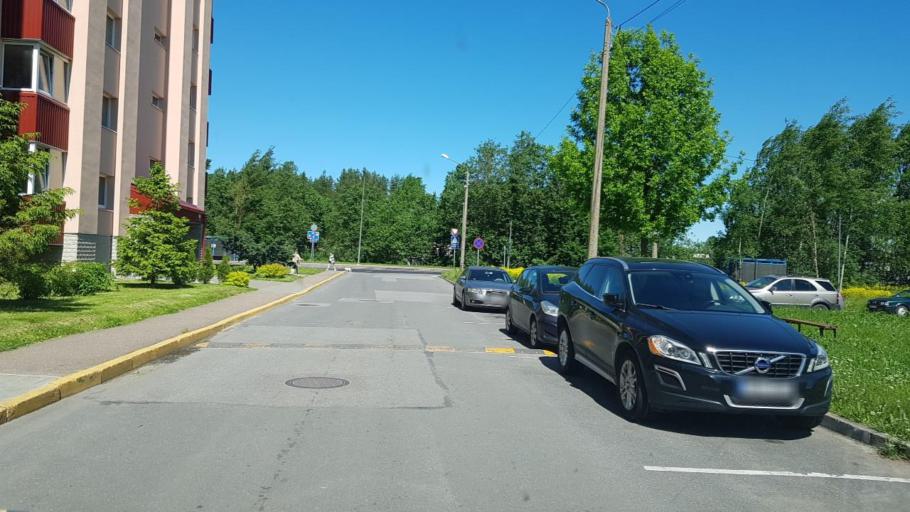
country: EE
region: Ida-Virumaa
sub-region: Narva linn
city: Narva
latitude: 59.3924
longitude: 28.1766
